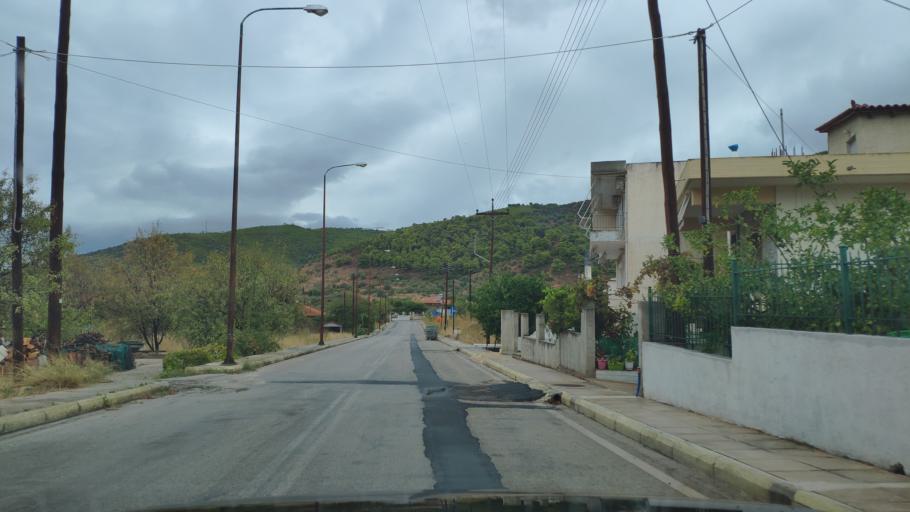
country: GR
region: Peloponnese
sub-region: Nomos Korinthias
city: Perachora
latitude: 38.0278
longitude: 22.9467
